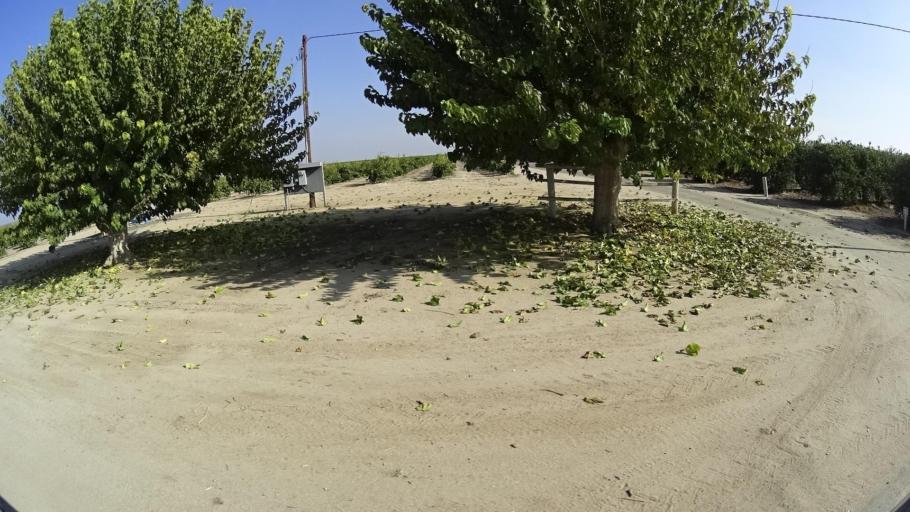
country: US
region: California
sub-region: Kern County
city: McFarland
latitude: 35.6056
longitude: -119.1866
